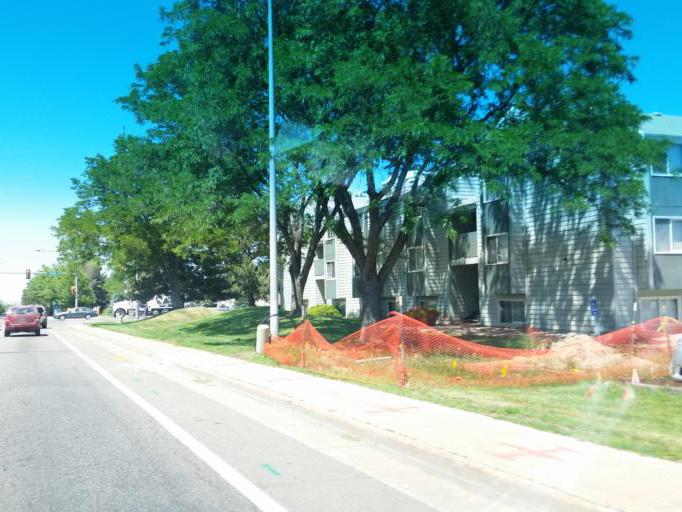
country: US
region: Colorado
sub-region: Larimer County
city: Fort Collins
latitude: 40.5519
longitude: -105.0960
